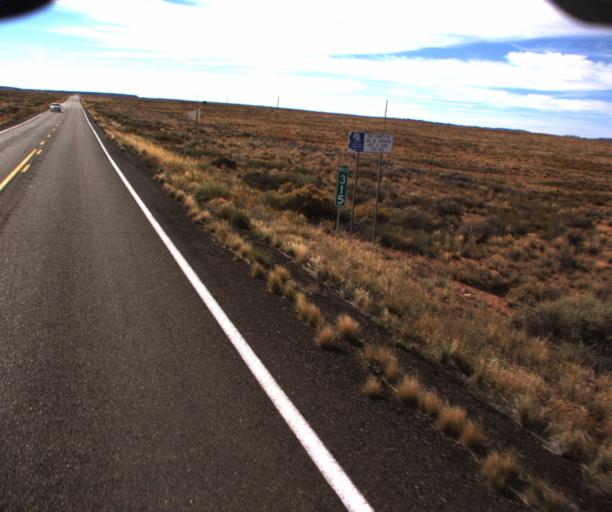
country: US
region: Arizona
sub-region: Coconino County
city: LeChee
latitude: 36.7217
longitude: -111.2776
